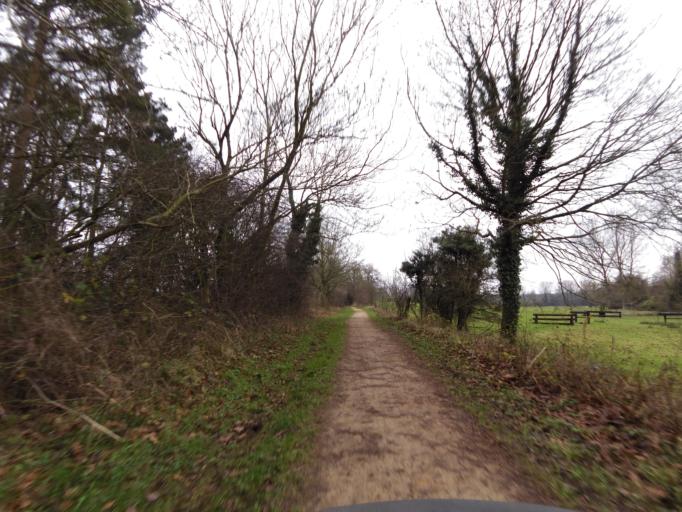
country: GB
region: England
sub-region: Norfolk
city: Mattishall
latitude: 52.7418
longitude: 1.0941
